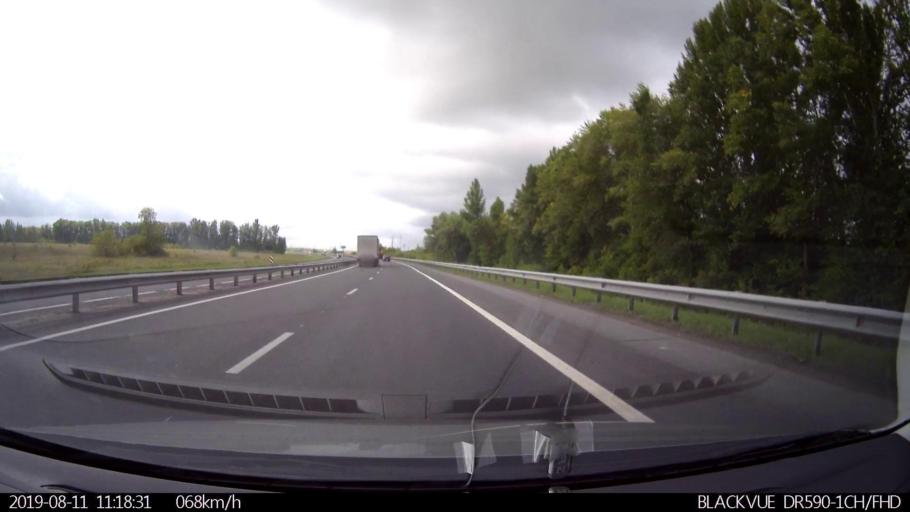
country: RU
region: Ulyanovsk
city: Novoul'yanovsk
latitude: 54.1791
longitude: 48.2676
